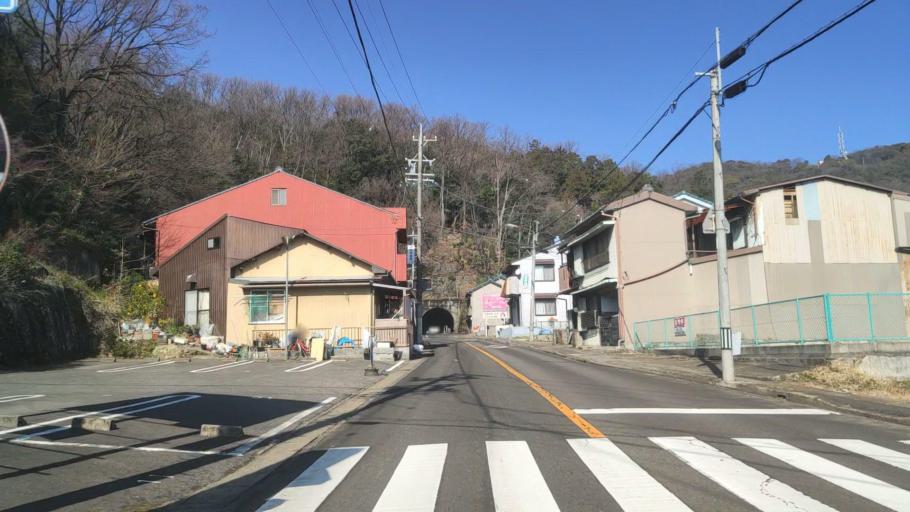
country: JP
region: Gifu
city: Gifu-shi
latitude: 35.4187
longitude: 136.7745
